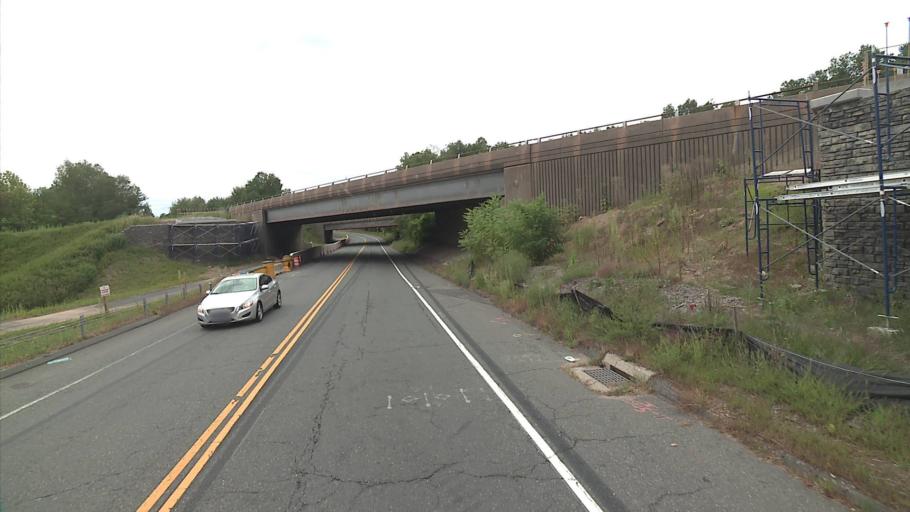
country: US
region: Connecticut
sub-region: Hartford County
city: Manchester
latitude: 41.7679
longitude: -72.4801
